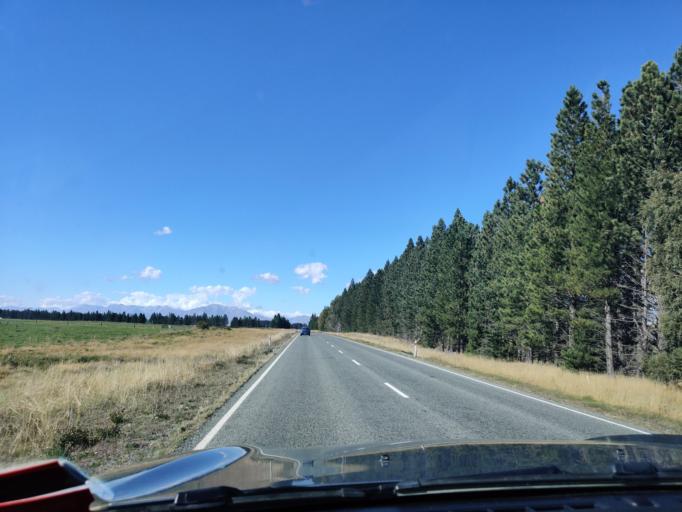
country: NZ
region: Canterbury
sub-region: Timaru District
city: Pleasant Point
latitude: -44.1890
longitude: 170.2978
